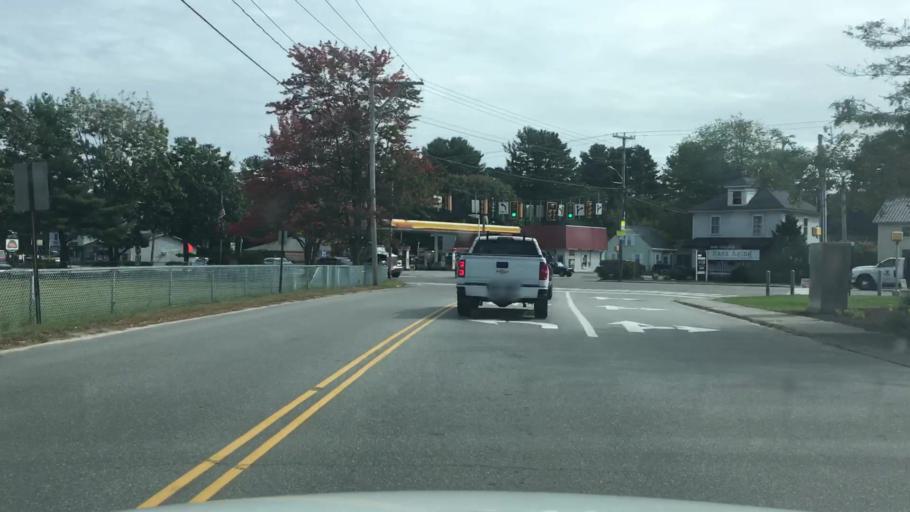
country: US
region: Maine
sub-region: Sagadahoc County
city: Topsham
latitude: 43.9132
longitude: -69.9810
